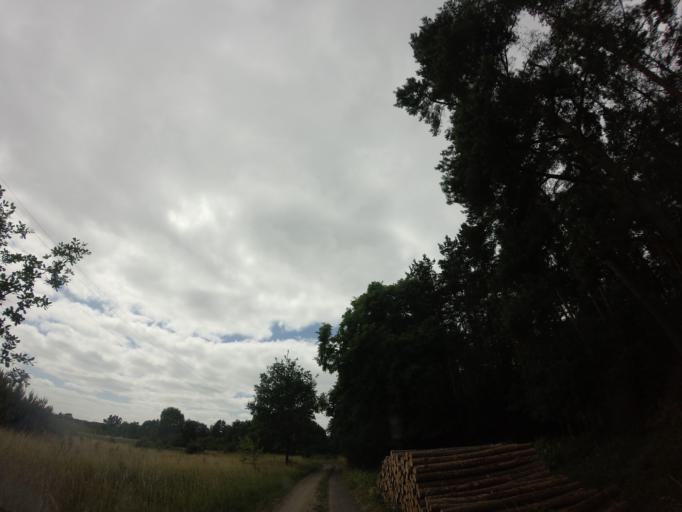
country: PL
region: West Pomeranian Voivodeship
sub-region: Powiat choszczenski
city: Krzecin
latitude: 53.0294
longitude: 15.5371
